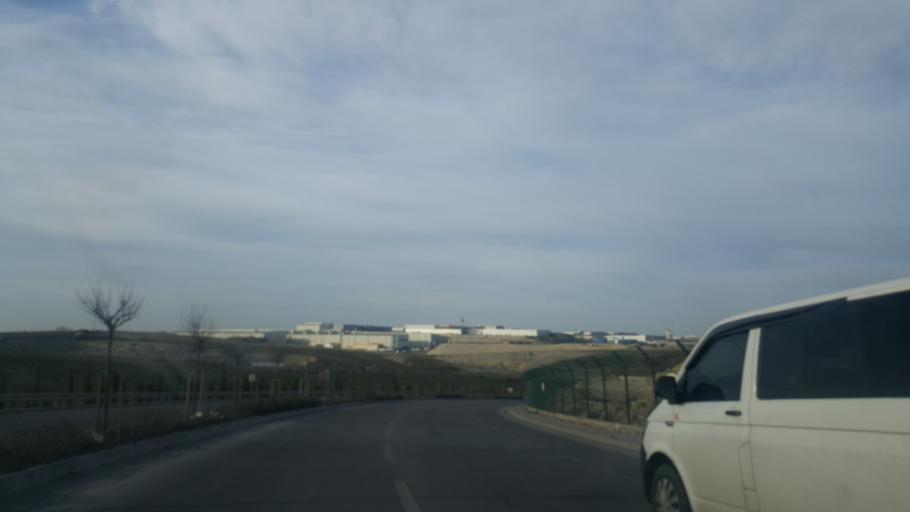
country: TR
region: Kocaeli
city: Tavsanli
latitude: 40.8232
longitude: 29.5587
